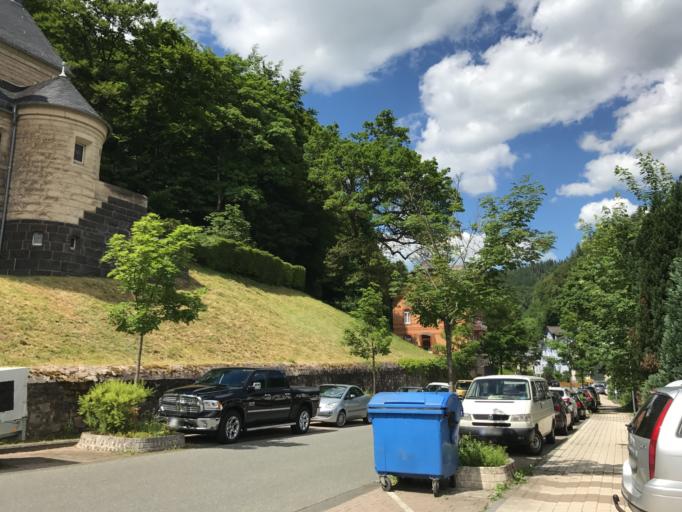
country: DE
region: Hesse
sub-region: Regierungsbezirk Darmstadt
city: Schlangenbad
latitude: 50.0949
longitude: 8.1036
